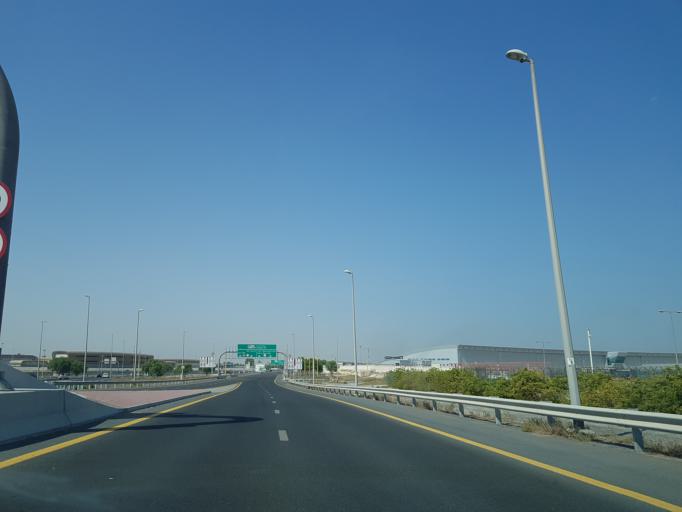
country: AE
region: Ash Shariqah
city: Sharjah
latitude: 25.2345
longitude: 55.4016
